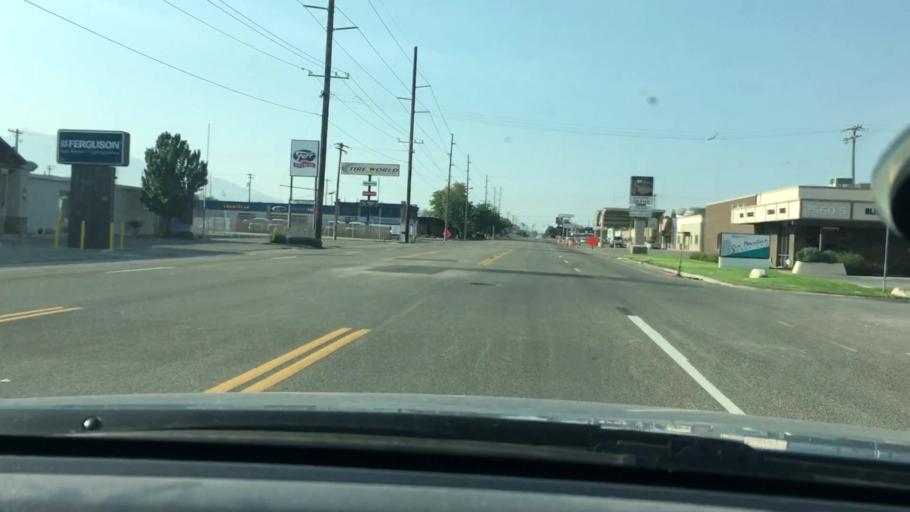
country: US
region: Utah
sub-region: Salt Lake County
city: South Salt Lake
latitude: 40.7159
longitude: -111.8998
